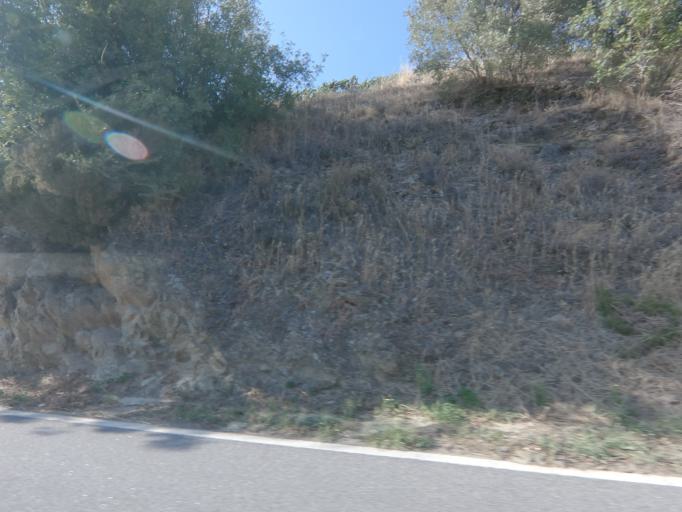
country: PT
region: Viseu
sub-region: Tabuaco
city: Tabuaco
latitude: 41.1346
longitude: -7.5715
